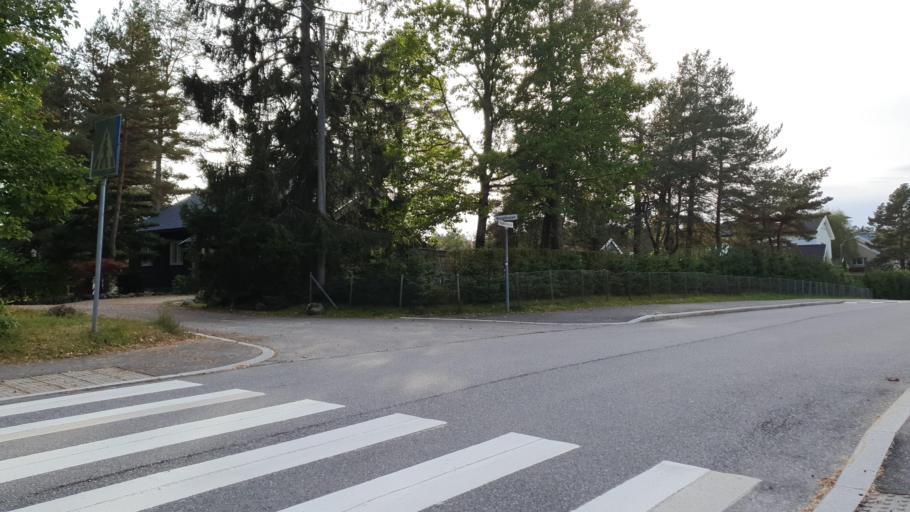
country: NO
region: Vestfold
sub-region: Tonsberg
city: Tonsberg
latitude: 59.2817
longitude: 10.4179
